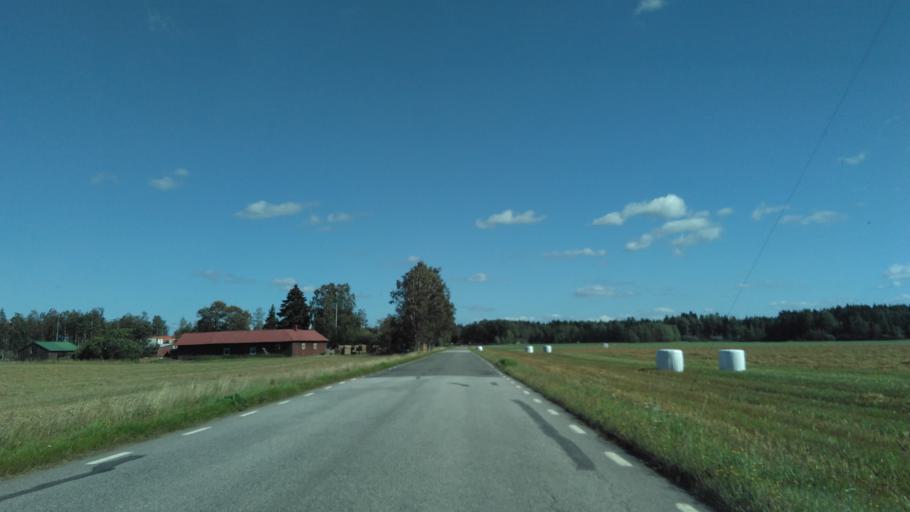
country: SE
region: Vaestra Goetaland
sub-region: Skara Kommun
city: Axvall
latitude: 58.3889
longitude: 13.5207
